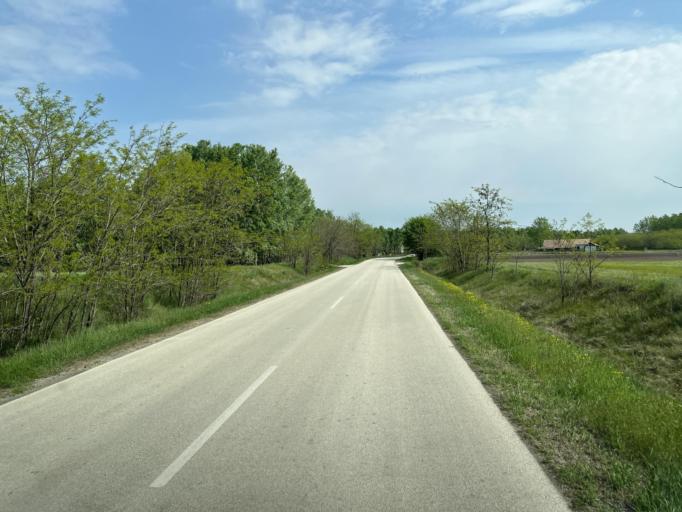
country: HU
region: Pest
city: Kocser
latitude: 47.0498
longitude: 19.9452
